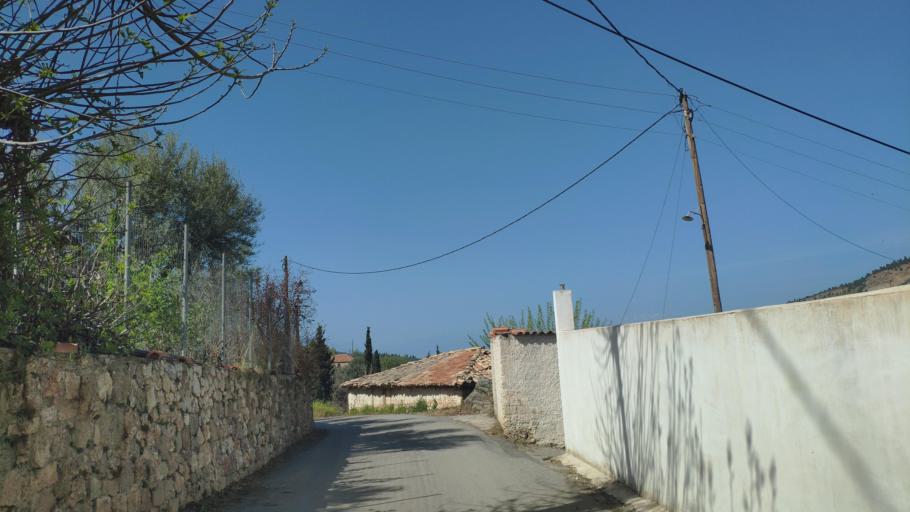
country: GR
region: West Greece
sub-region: Nomos Achaias
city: Aiyira
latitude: 38.0805
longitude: 22.3377
